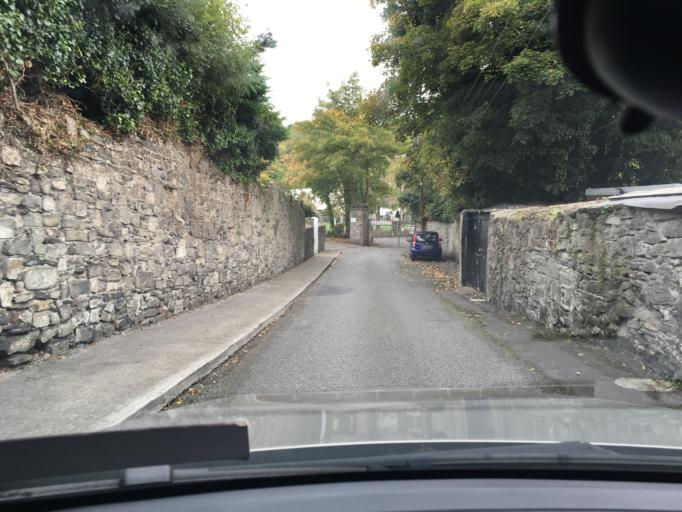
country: IE
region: Leinster
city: Ballyfermot
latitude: 53.3574
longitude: -6.3613
